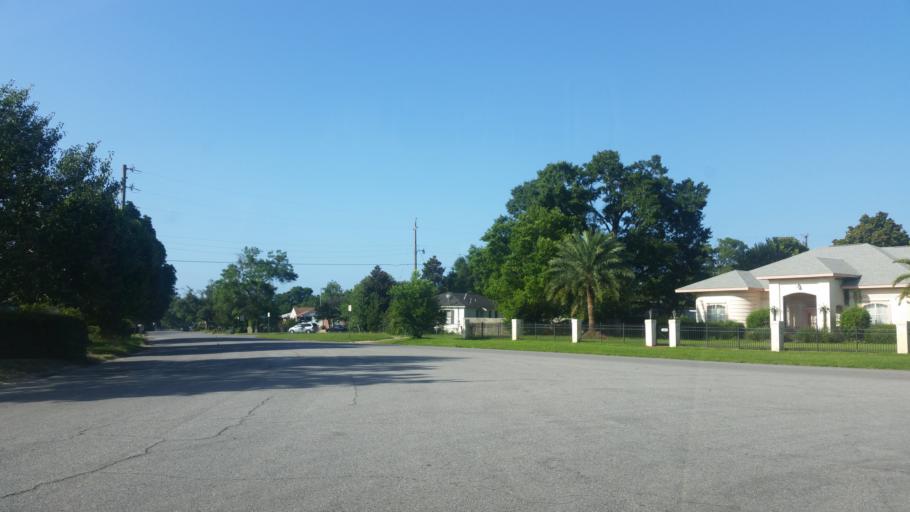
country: US
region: Florida
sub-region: Escambia County
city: Warrington
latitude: 30.3787
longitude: -87.2888
